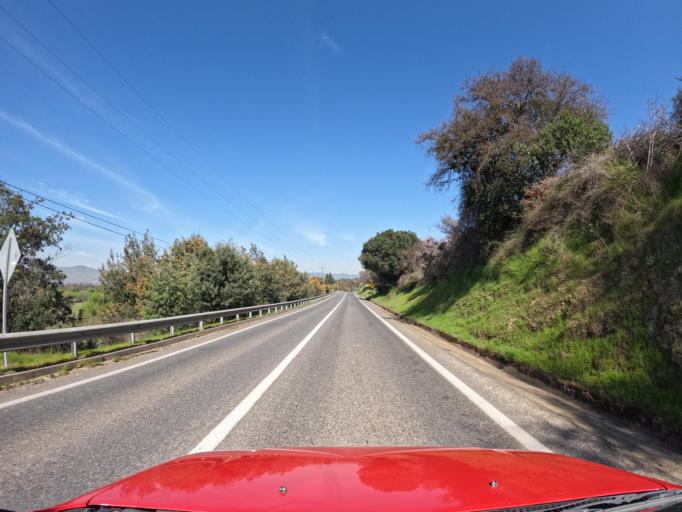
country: CL
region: Maule
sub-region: Provincia de Curico
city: Rauco
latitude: -35.0583
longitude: -71.6160
